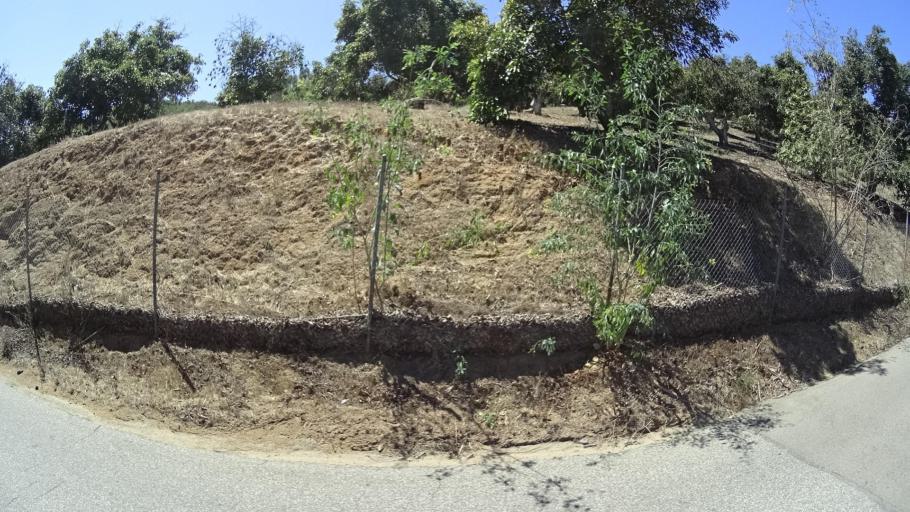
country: US
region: California
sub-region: San Diego County
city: Rainbow
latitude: 33.3440
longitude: -117.1724
